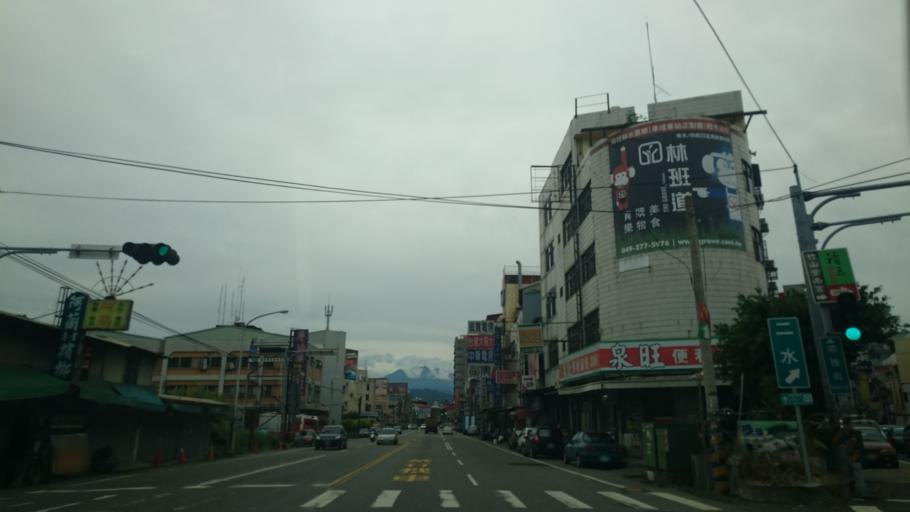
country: TW
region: Taiwan
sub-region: Nantou
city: Nantou
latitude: 23.8392
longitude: 120.7020
